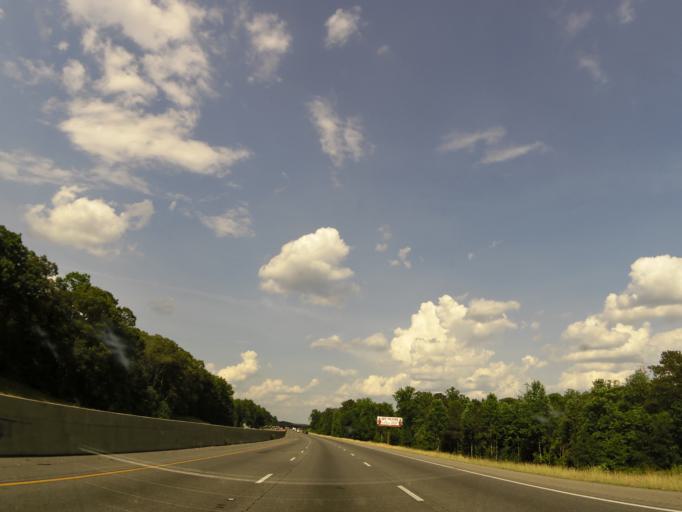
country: US
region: Alabama
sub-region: Tuscaloosa County
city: Coaling
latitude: 33.1783
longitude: -87.3769
